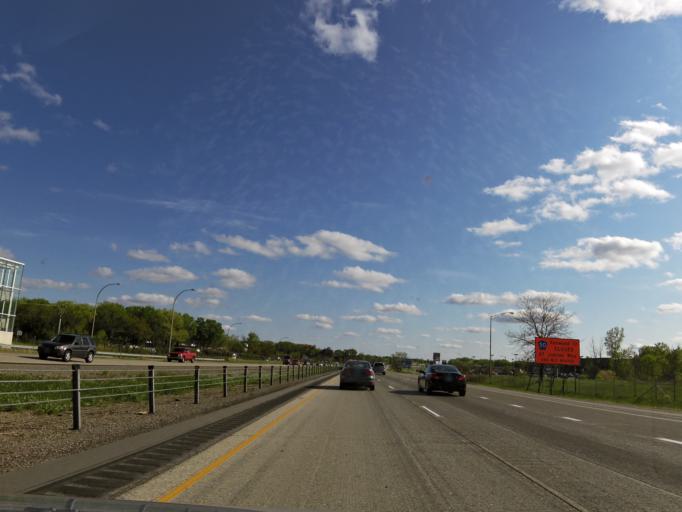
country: US
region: Minnesota
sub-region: Dakota County
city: Burnsville
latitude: 44.7060
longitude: -93.2851
